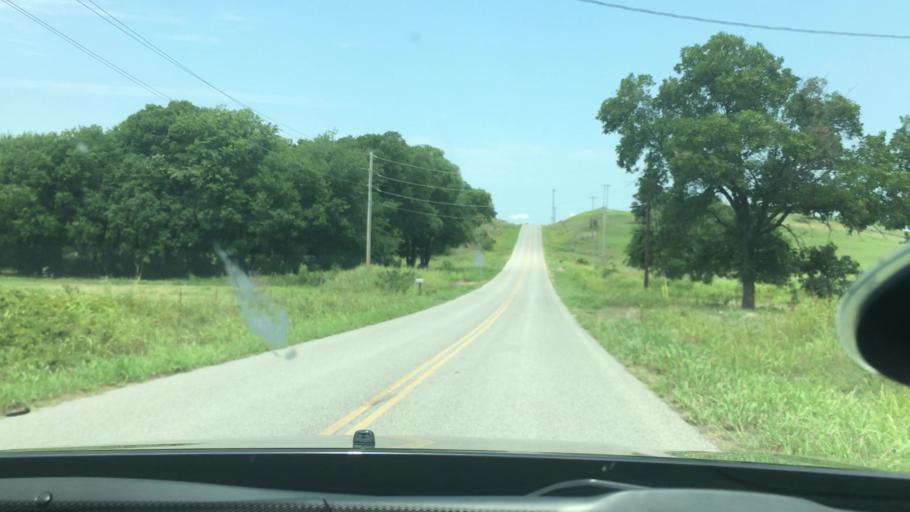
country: US
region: Oklahoma
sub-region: Love County
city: Marietta
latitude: 33.9249
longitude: -97.3521
